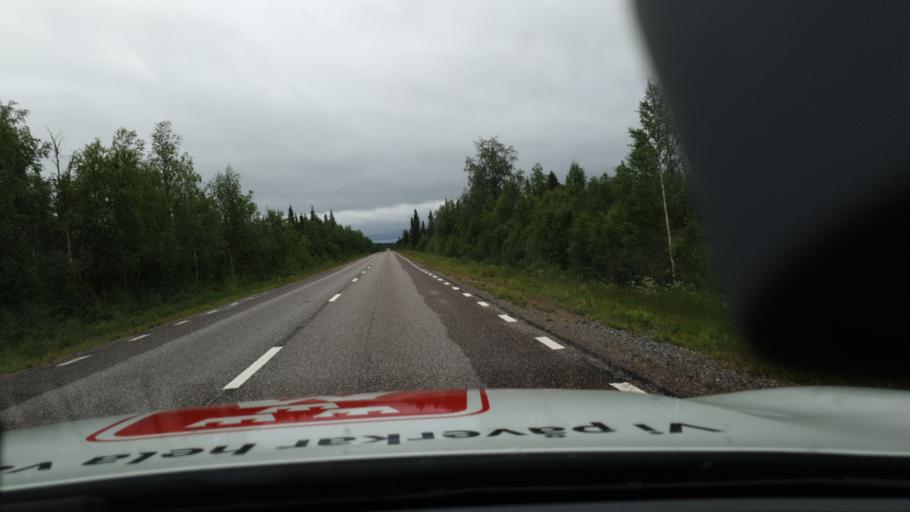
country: SE
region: Norrbotten
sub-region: Pajala Kommun
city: Pajala
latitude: 67.1312
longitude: 23.5880
